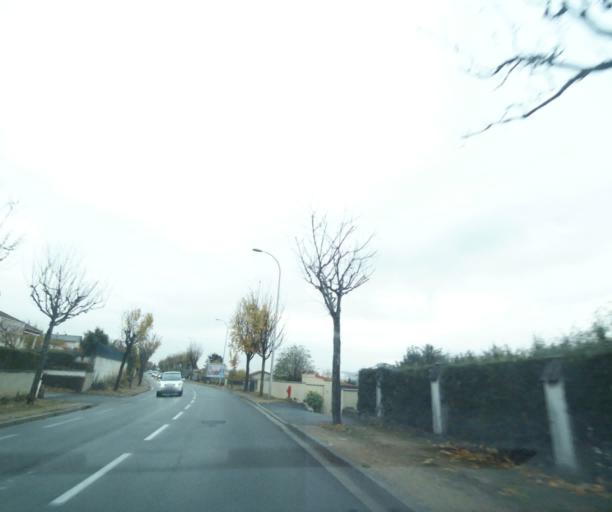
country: FR
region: Auvergne
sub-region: Departement du Puy-de-Dome
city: Cournon-d'Auvergne
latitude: 45.7411
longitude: 3.1842
